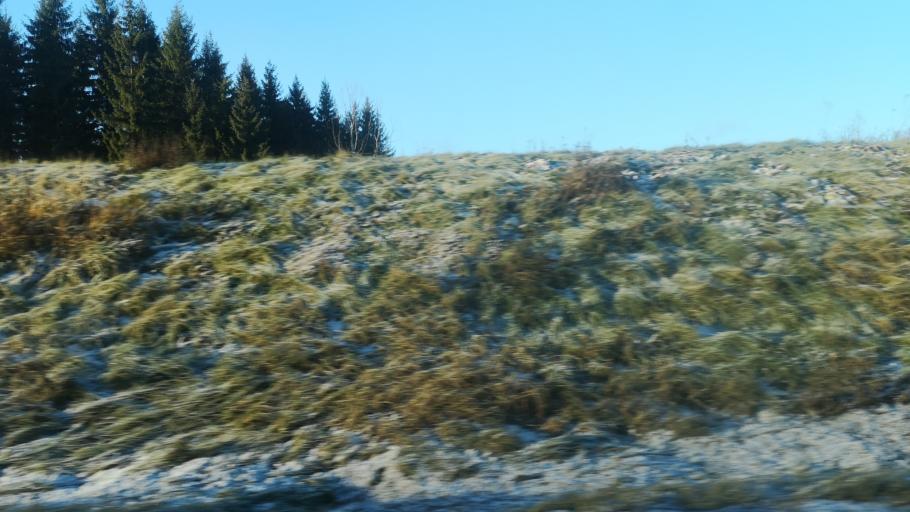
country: FI
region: Paijanne Tavastia
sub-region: Lahti
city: Nastola
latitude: 61.0849
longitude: 25.8943
